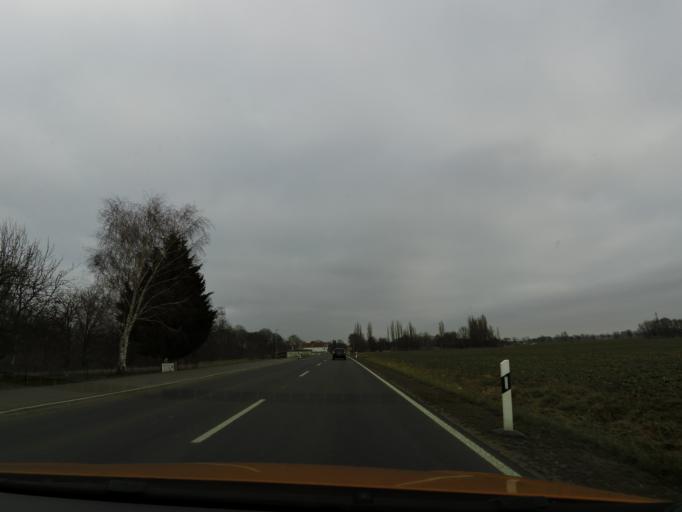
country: DE
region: Brandenburg
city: Walsleben
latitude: 52.8770
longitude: 12.6198
